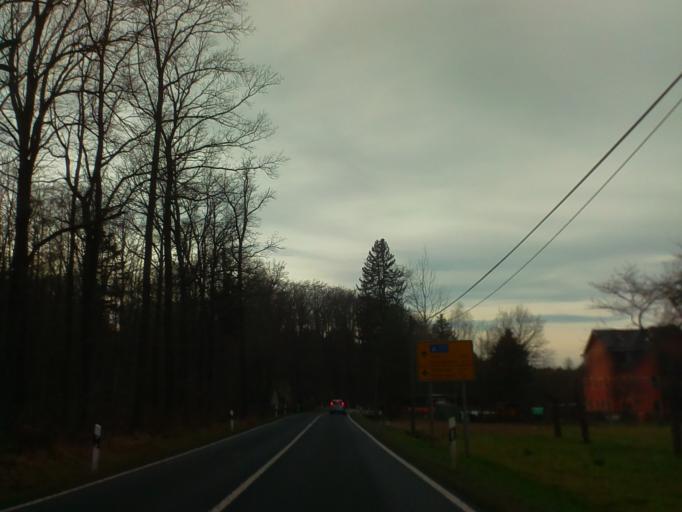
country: DE
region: Thuringia
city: Albersdorf
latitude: 50.8951
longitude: 11.7766
